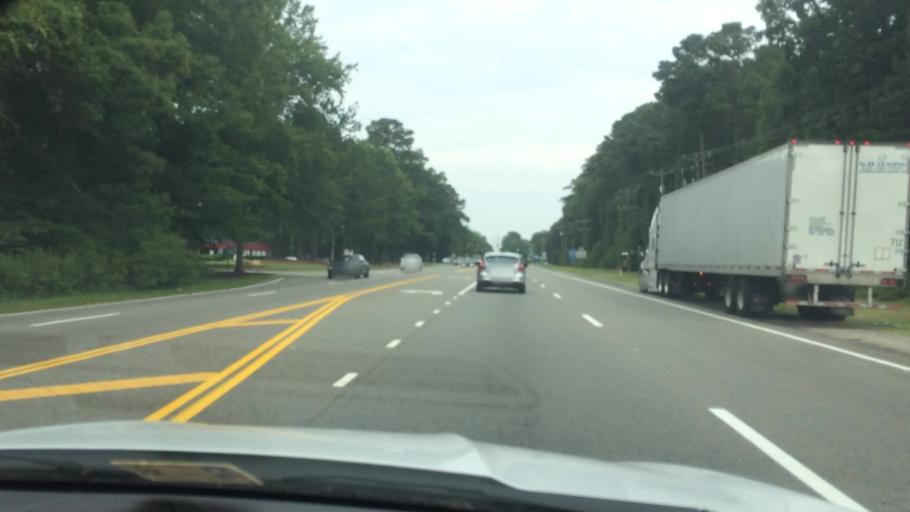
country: US
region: Virginia
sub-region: York County
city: Yorktown
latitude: 37.1726
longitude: -76.5467
